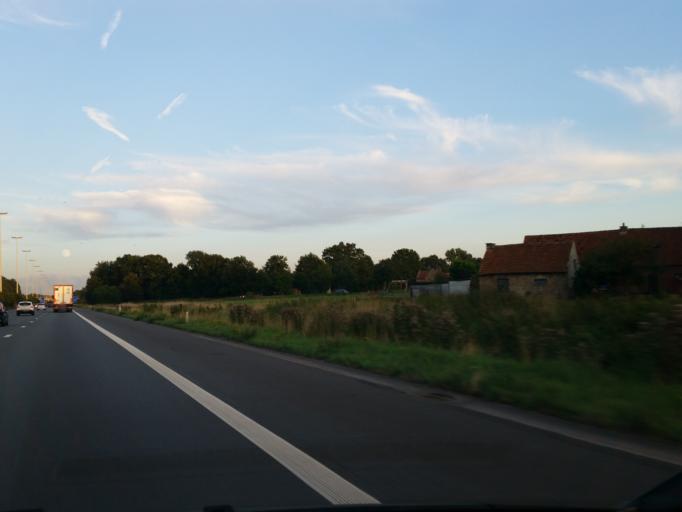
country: BE
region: Flanders
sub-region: Provincie West-Vlaanderen
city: Beernem
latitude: 51.1295
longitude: 3.2939
